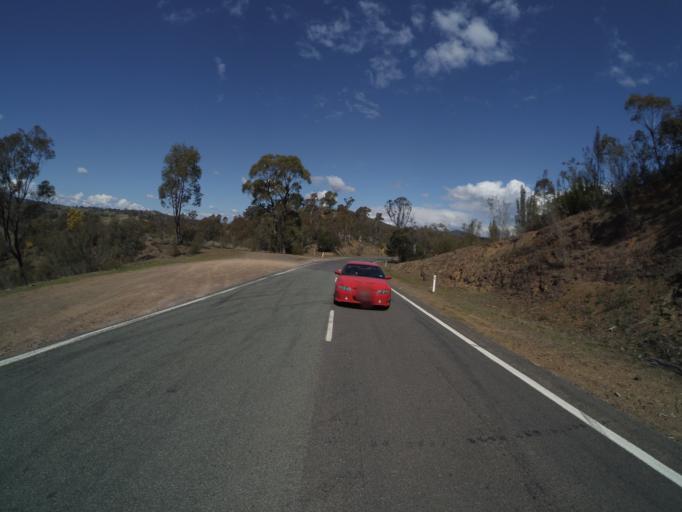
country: AU
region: Australian Capital Territory
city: Macquarie
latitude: -35.3201
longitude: 148.9453
